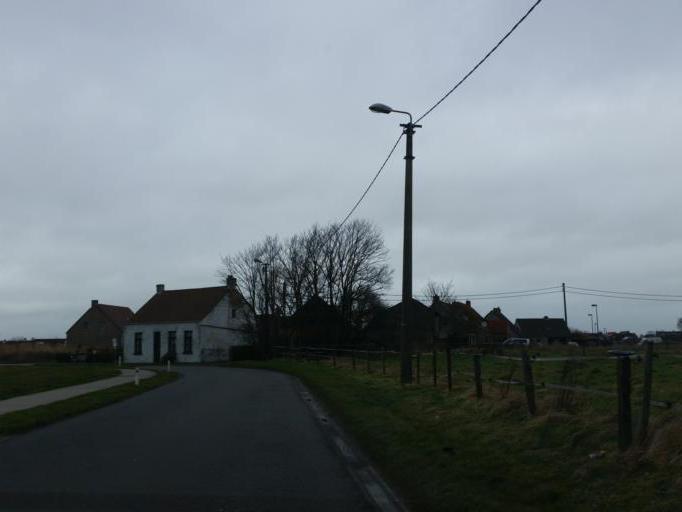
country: BE
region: Flanders
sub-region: Provincie West-Vlaanderen
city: Bredene
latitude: 51.2450
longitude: 2.9876
